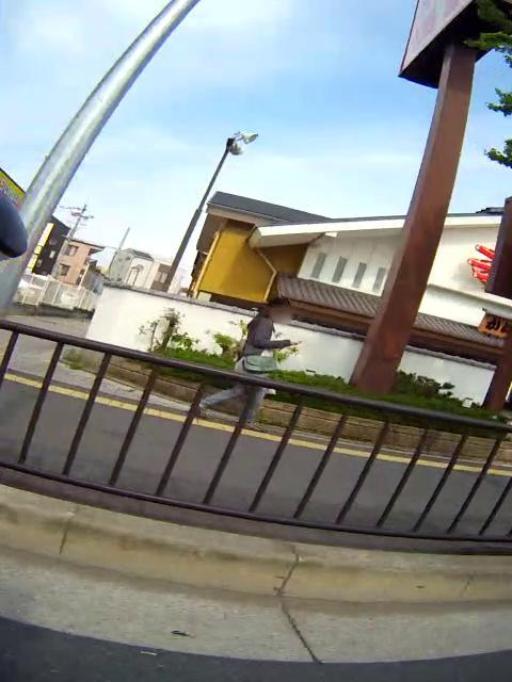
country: JP
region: Osaka
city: Toyonaka
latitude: 34.8032
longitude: 135.4713
